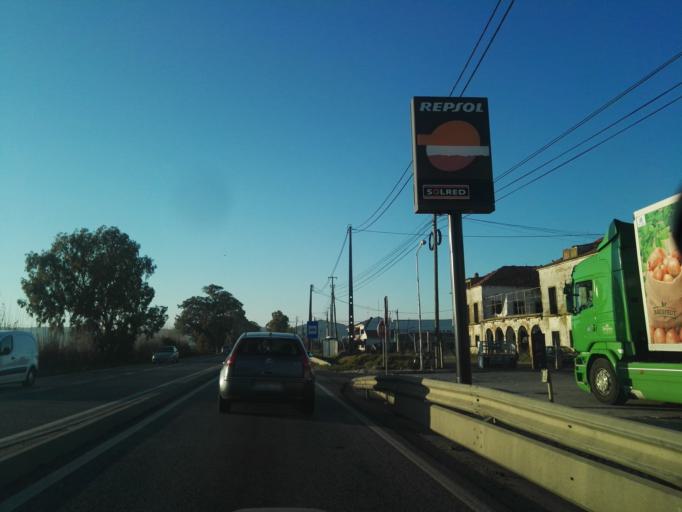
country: PT
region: Lisbon
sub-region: Vila Franca de Xira
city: Vila Franca de Xira
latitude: 38.9424
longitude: -8.9457
